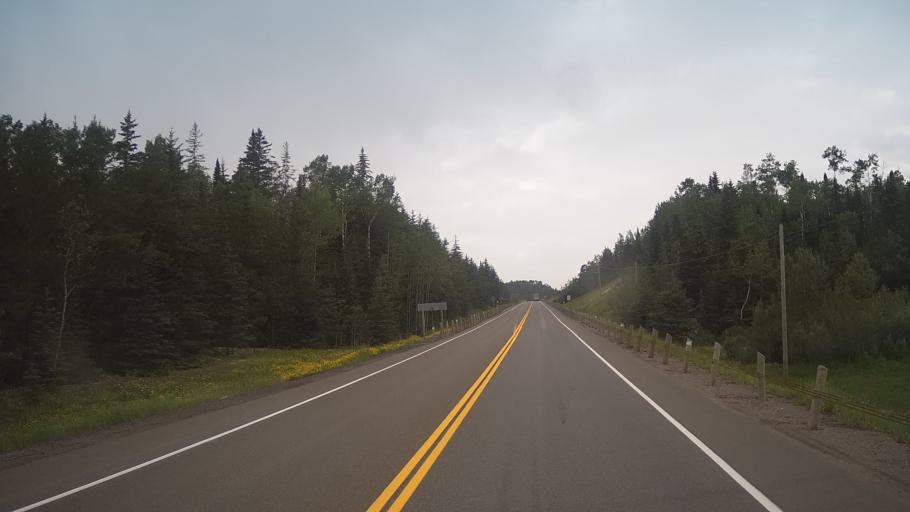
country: CA
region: Ontario
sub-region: Thunder Bay District
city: Thunder Bay
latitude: 48.5337
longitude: -89.5881
